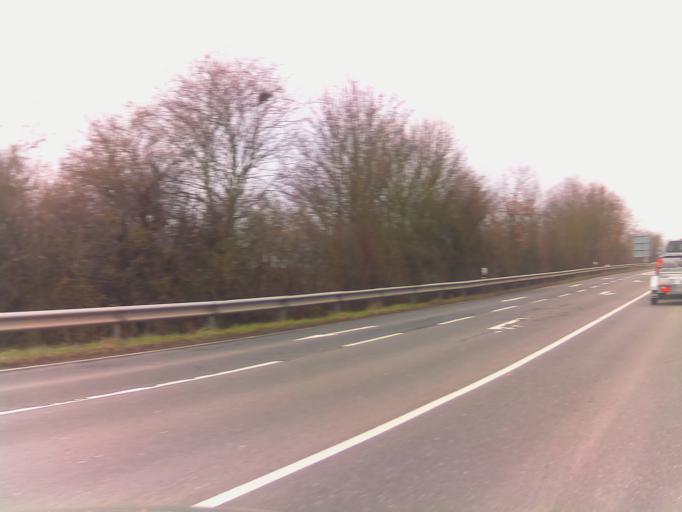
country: DE
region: Rheinland-Pfalz
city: Kongernheim
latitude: 49.8437
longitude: 8.2428
